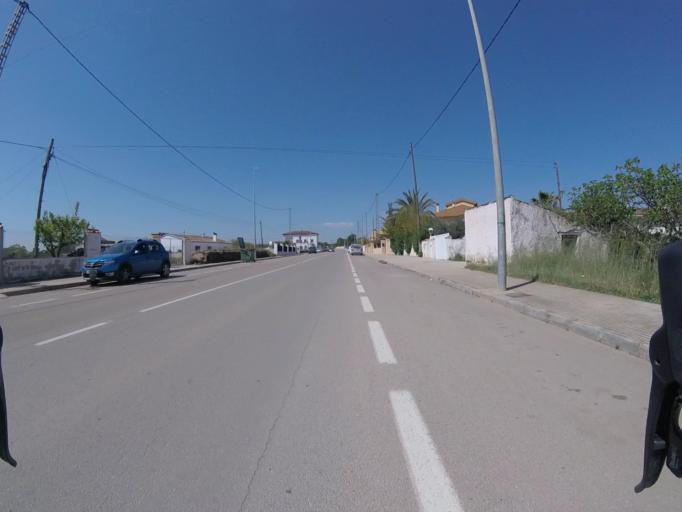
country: ES
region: Valencia
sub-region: Provincia de Castello
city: Benlloch
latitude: 40.2092
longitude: 0.0228
